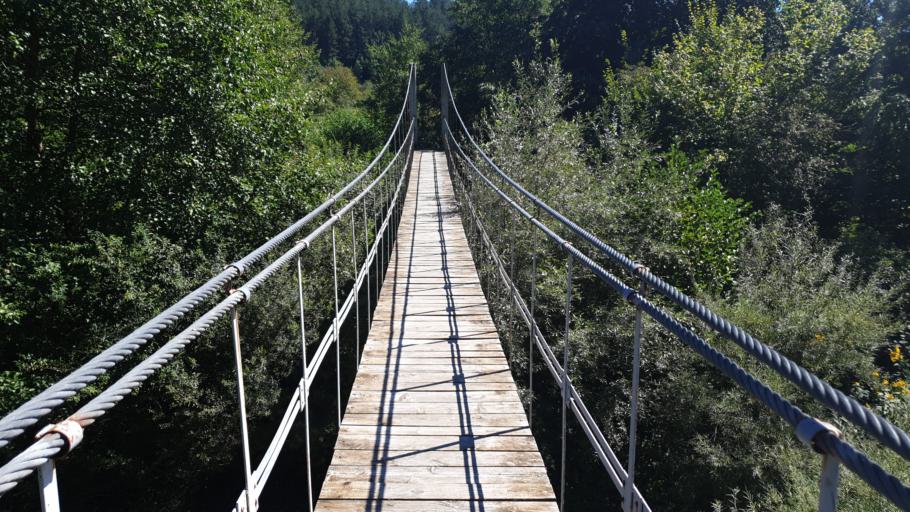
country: BA
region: Federation of Bosnia and Herzegovina
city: Polje-Bijela
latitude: 43.5282
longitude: 18.0800
